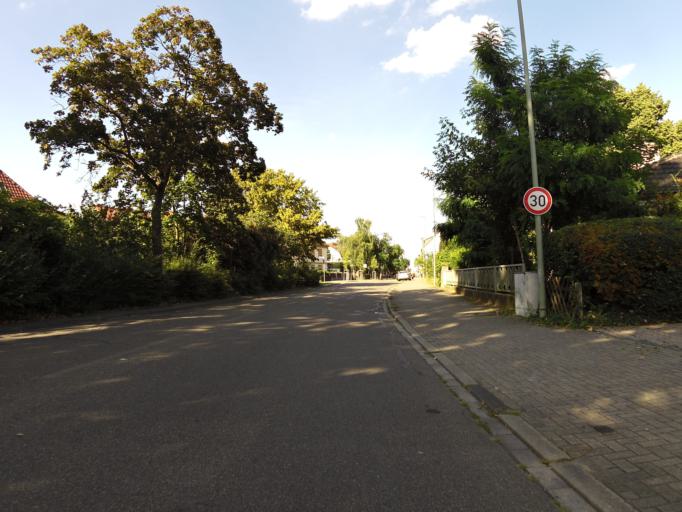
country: DE
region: Rheinland-Pfalz
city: Gartenstadt
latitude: 49.4863
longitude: 8.3689
